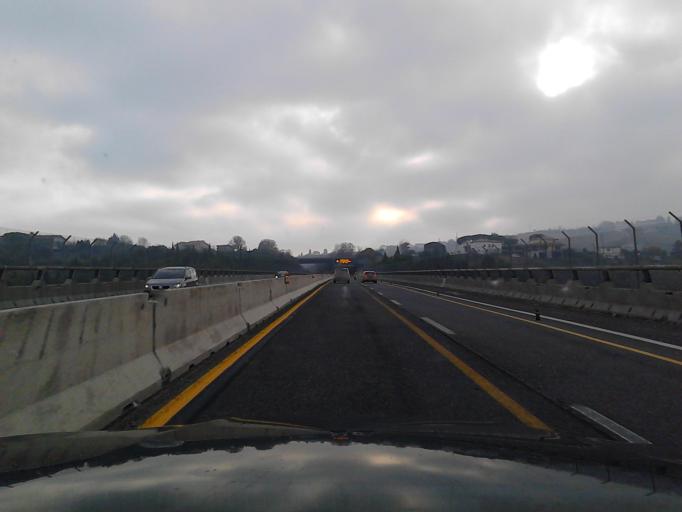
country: IT
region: Abruzzo
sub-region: Provincia di Teramo
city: Salino
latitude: 42.7743
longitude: 13.9312
